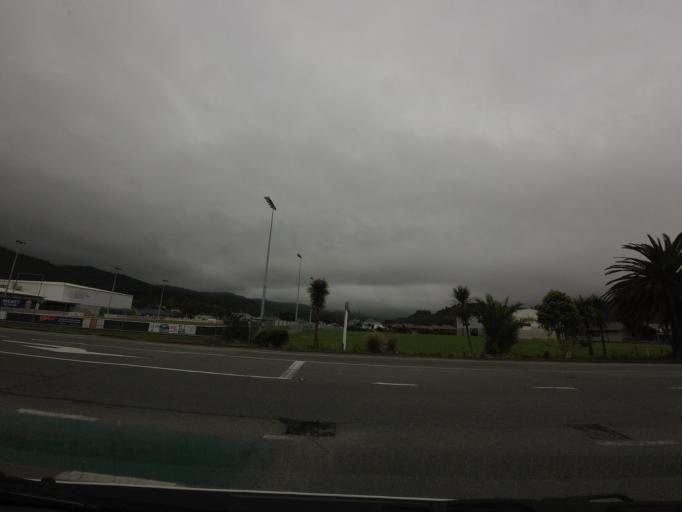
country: NZ
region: West Coast
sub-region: Grey District
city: Greymouth
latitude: -42.4613
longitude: 171.1985
